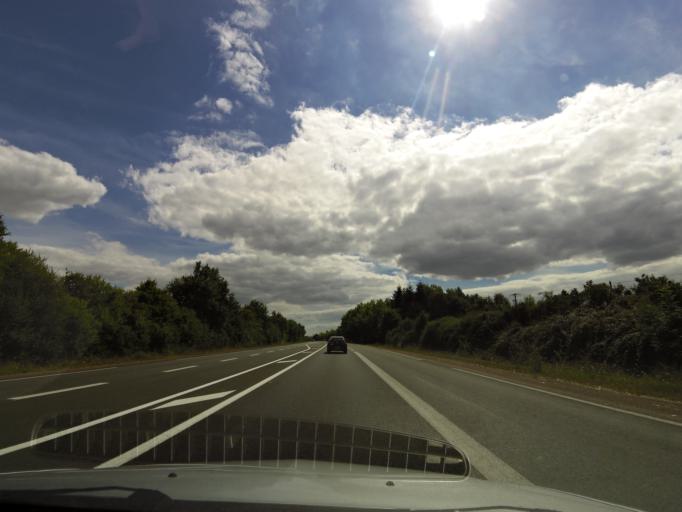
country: FR
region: Pays de la Loire
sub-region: Departement de la Vendee
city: Aubigny
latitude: 46.5850
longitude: -1.4489
